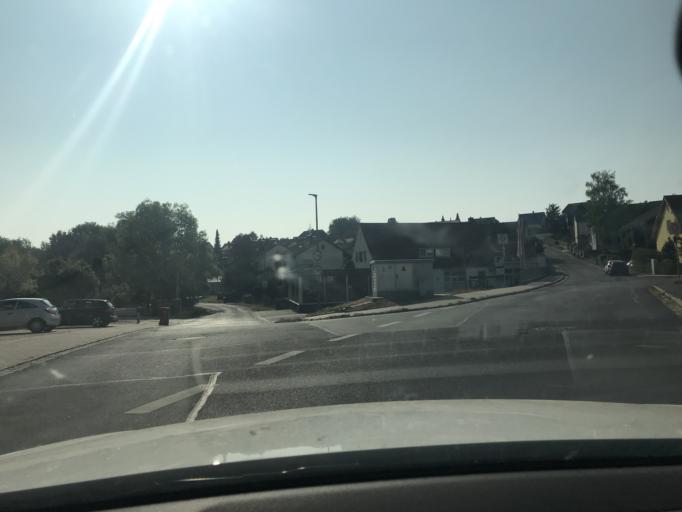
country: DE
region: Bavaria
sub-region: Upper Franconia
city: Pegnitz
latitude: 49.7512
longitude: 11.5442
